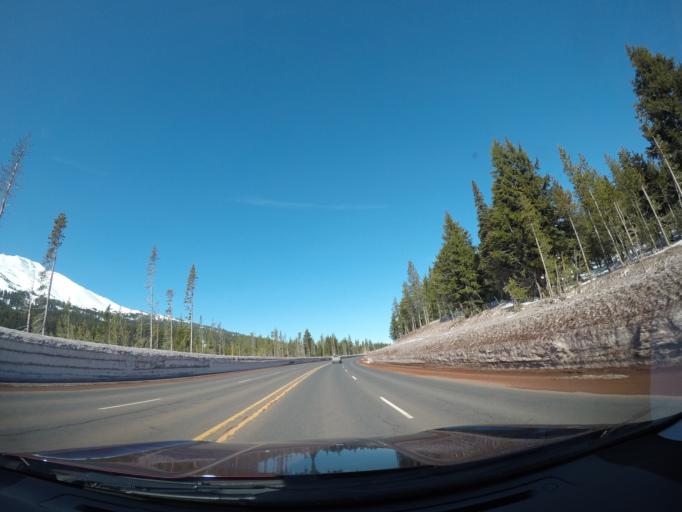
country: US
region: Oregon
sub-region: Deschutes County
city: Sunriver
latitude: 43.9907
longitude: -121.6540
